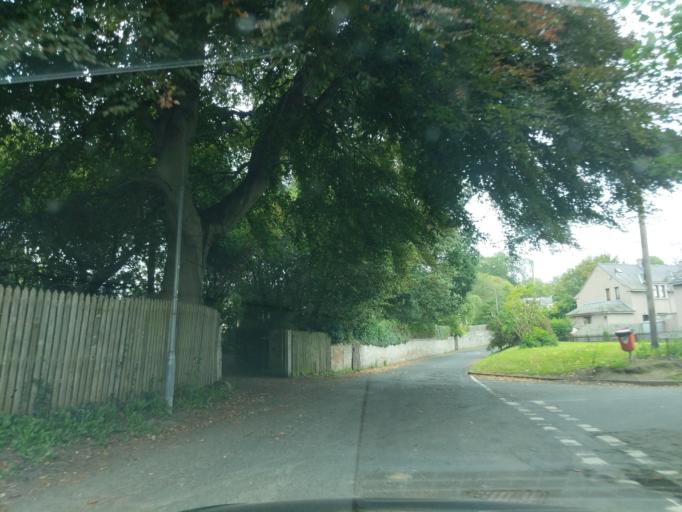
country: GB
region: Scotland
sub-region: The Scottish Borders
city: Saint Boswells
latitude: 55.5716
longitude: -2.6384
